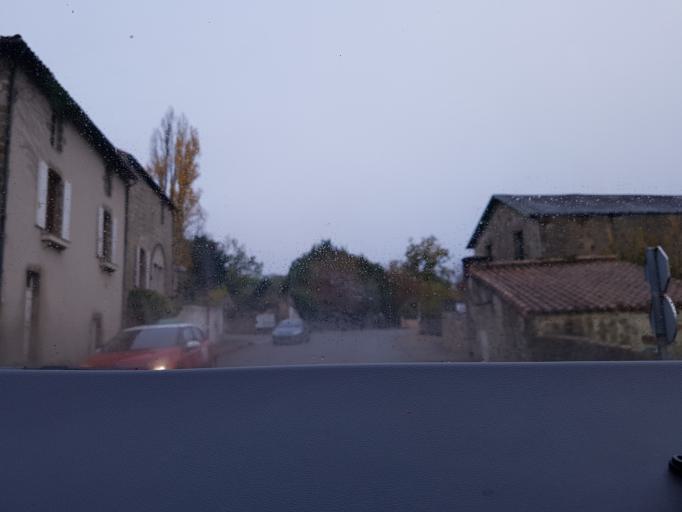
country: FR
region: Poitou-Charentes
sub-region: Departement des Deux-Sevres
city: Parthenay
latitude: 46.6546
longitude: -0.2481
